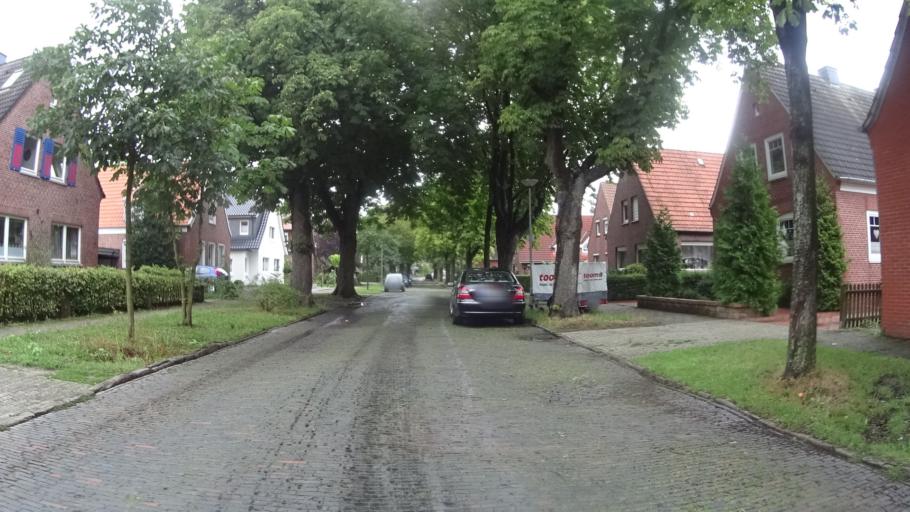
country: DE
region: Lower Saxony
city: Leer
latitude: 53.2338
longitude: 7.4452
